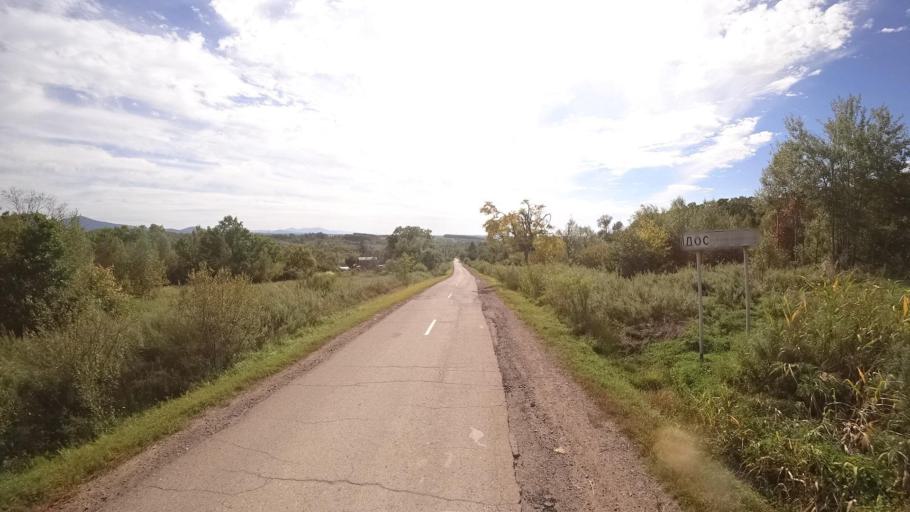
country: RU
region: Primorskiy
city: Dostoyevka
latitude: 44.3363
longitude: 133.4864
